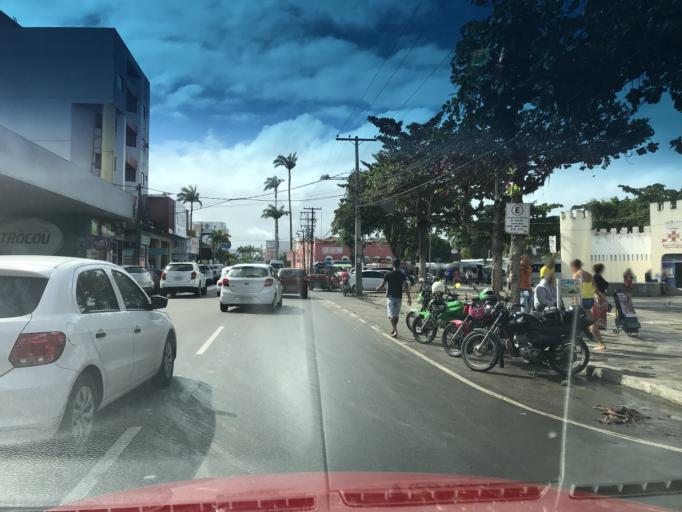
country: BR
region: Bahia
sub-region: Santo Antonio De Jesus
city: Santo Antonio de Jesus
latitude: -12.9663
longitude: -39.2673
